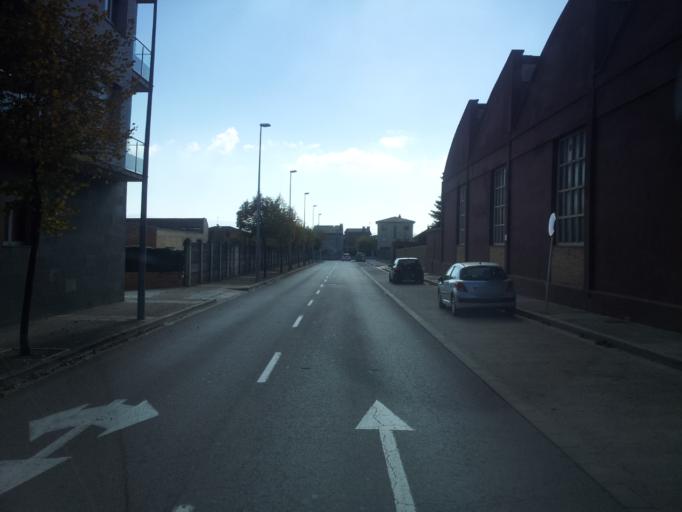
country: ES
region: Catalonia
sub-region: Provincia de Barcelona
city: Vic
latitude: 41.9287
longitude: 2.2432
